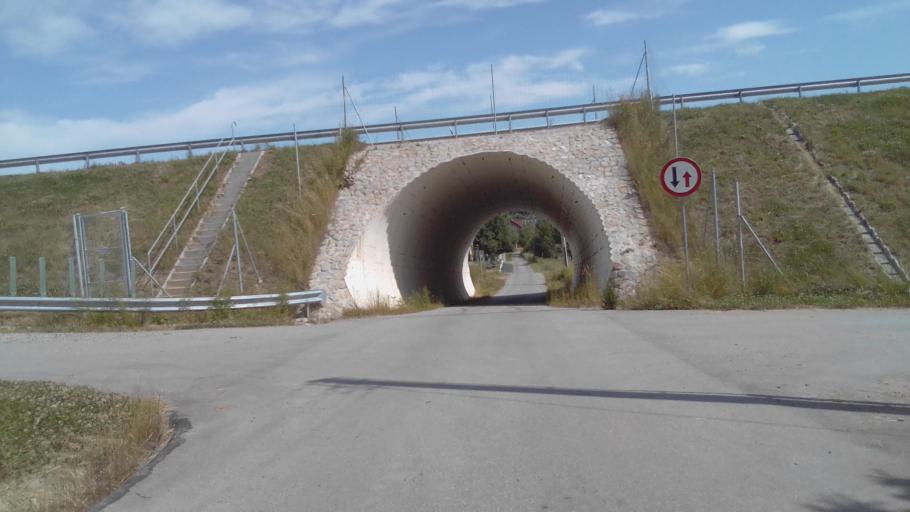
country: PL
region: Subcarpathian Voivodeship
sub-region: Powiat strzyzowski
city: Strzyzow
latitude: 49.8617
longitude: 21.8054
